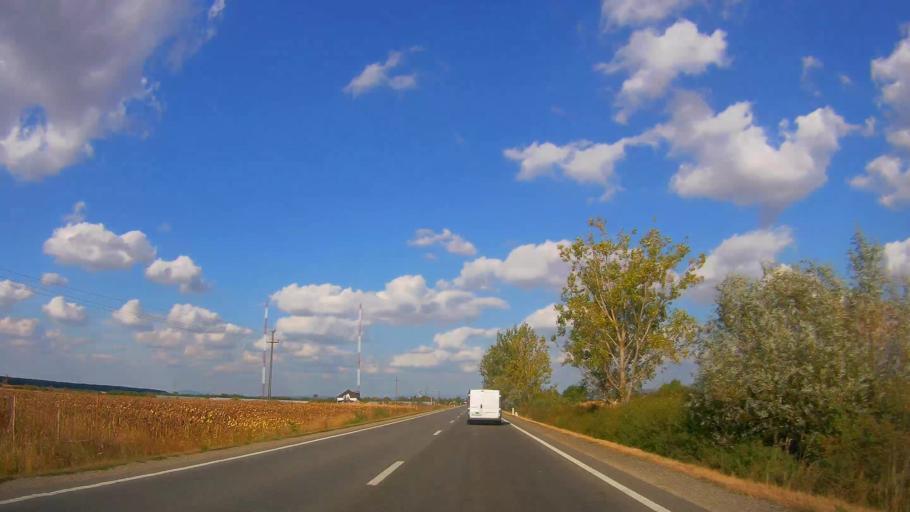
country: RO
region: Satu Mare
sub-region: Comuna Botiz
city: Botiz
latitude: 47.8486
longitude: 22.9699
